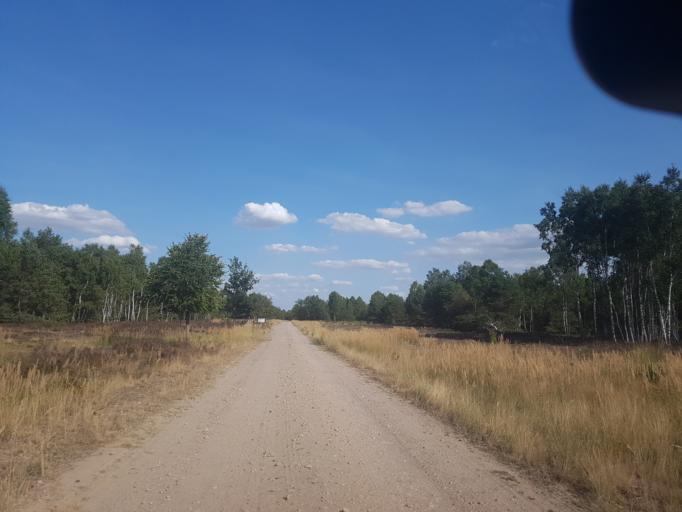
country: DE
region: Saxony-Anhalt
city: Seyda
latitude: 51.8721
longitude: 12.9880
